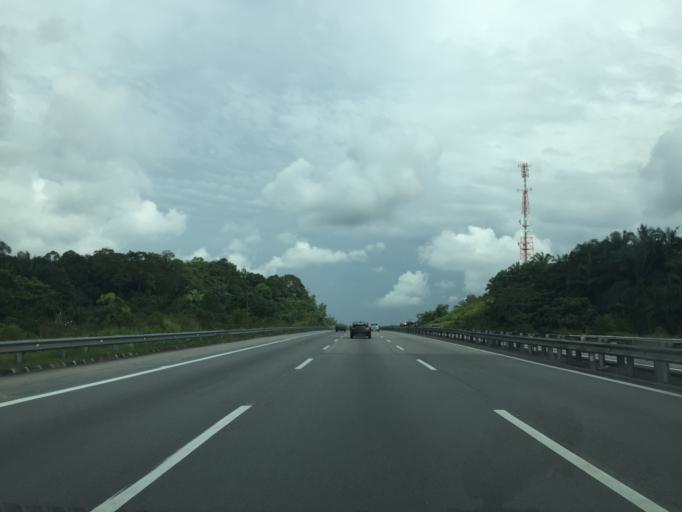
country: MY
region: Selangor
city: Batang Berjuntai
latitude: 3.6049
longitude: 101.5225
